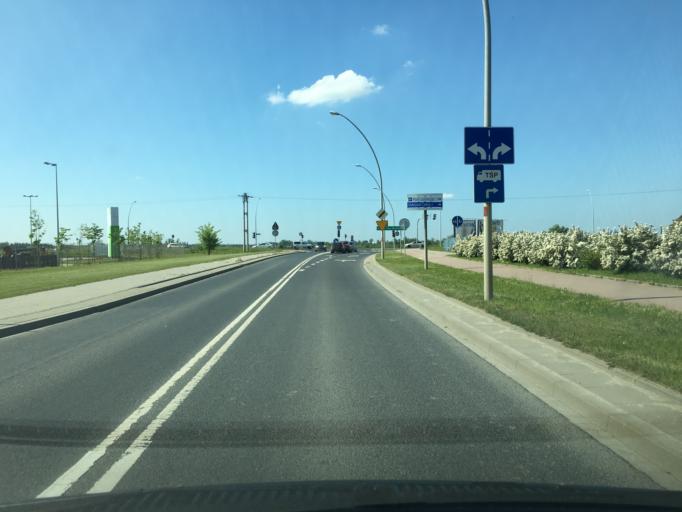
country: PL
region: Lower Silesian Voivodeship
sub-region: Powiat wroclawski
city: Bielany Wroclawskie
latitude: 51.0756
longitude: 16.9504
